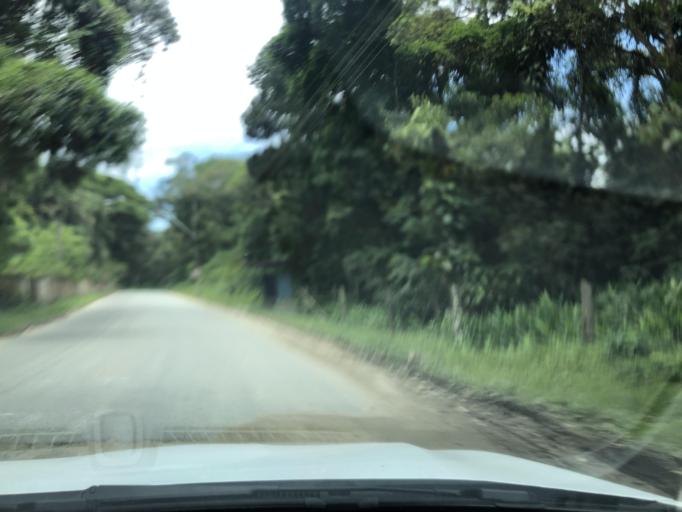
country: BR
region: Santa Catarina
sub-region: Sao Francisco Do Sul
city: Sao Francisco do Sul
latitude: -26.2270
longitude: -48.6020
